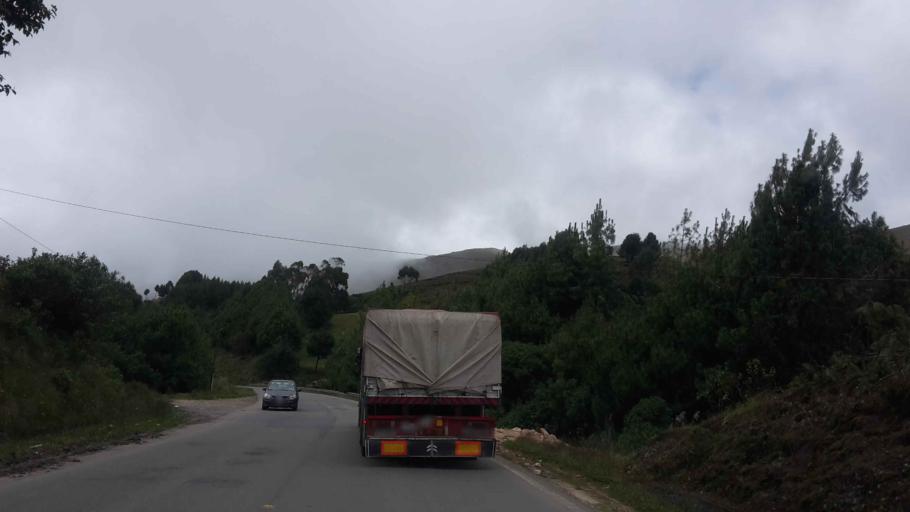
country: BO
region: Cochabamba
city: Colomi
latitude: -17.2481
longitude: -65.8914
